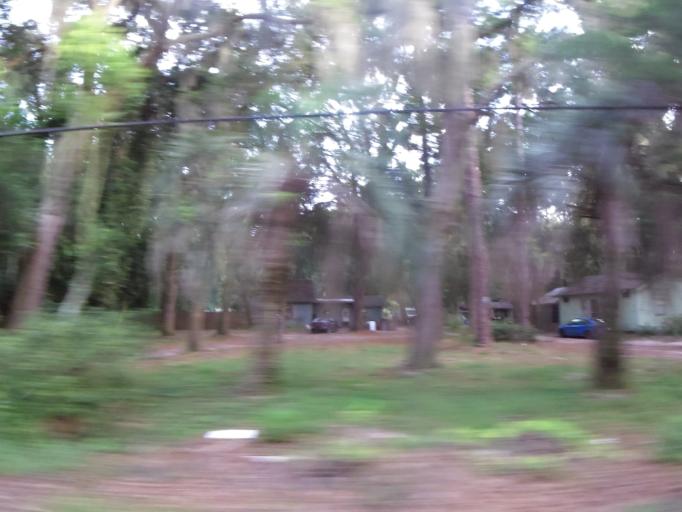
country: US
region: Florida
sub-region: Duval County
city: Jacksonville
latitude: 30.4175
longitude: -81.7258
